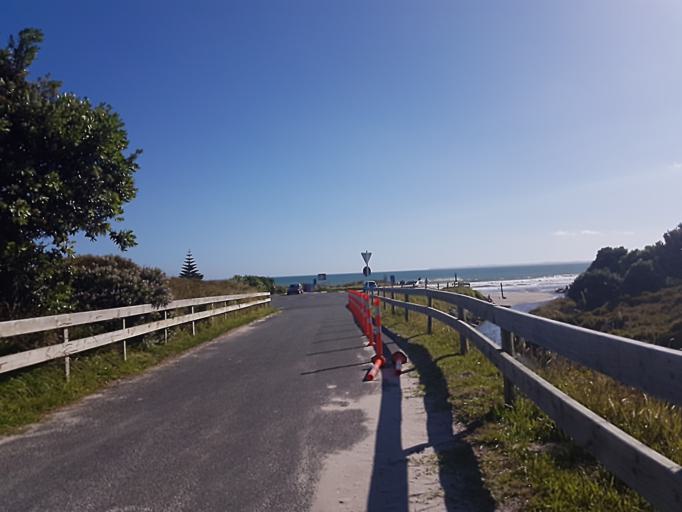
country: NZ
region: Bay of Plenty
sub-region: Tauranga City
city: Tauranga
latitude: -37.6912
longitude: 176.2728
